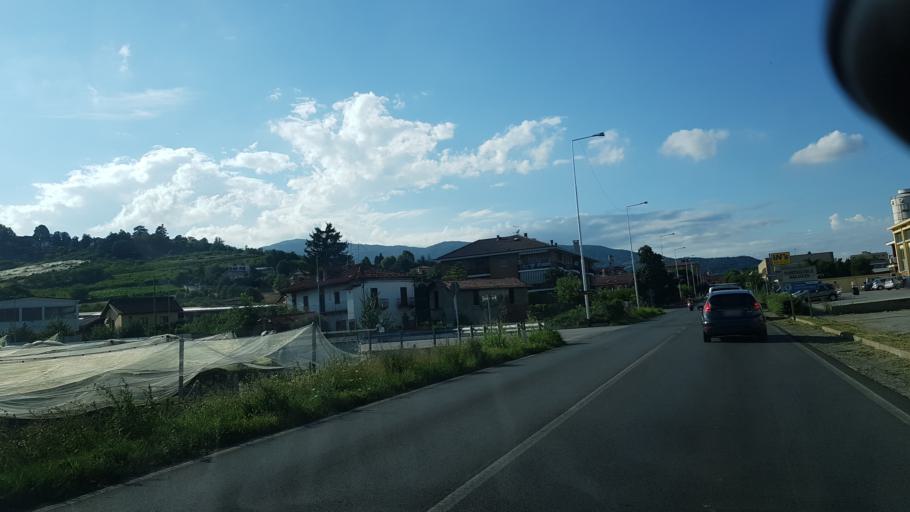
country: IT
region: Piedmont
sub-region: Provincia di Cuneo
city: Costiglione Saluzzo
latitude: 44.5570
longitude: 7.4898
